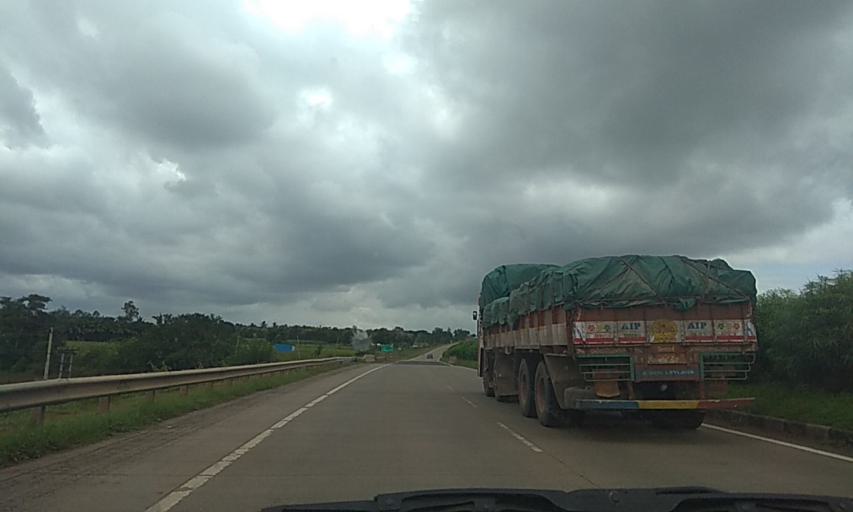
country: IN
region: Karnataka
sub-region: Belgaum
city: Sankeshwar
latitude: 16.2504
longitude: 74.4764
